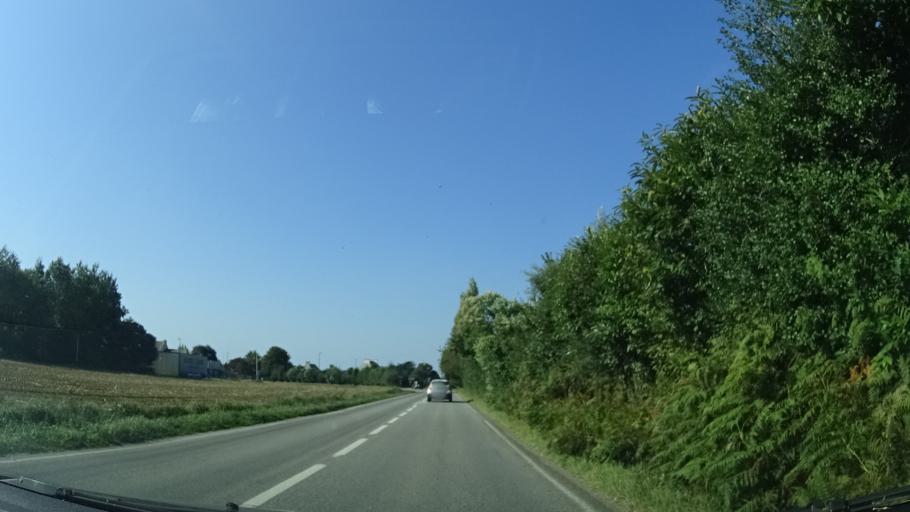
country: FR
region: Brittany
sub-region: Departement du Finistere
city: Plonevez-Porzay
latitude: 48.0921
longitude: -4.2631
